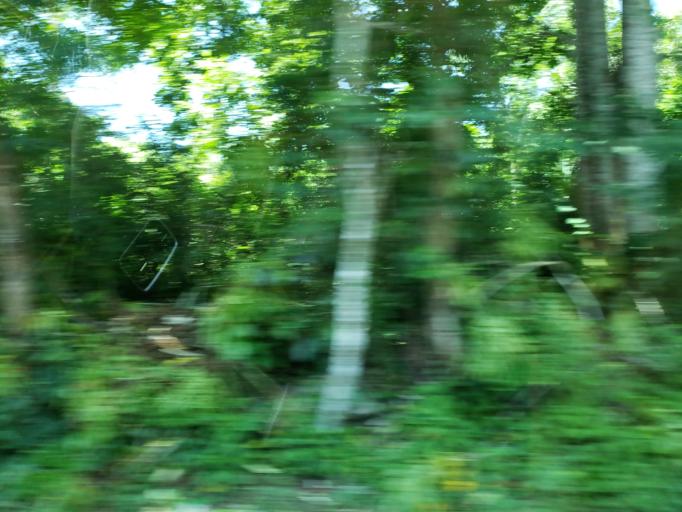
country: ID
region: Bali
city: Kangin
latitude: -8.8312
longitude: 115.1357
